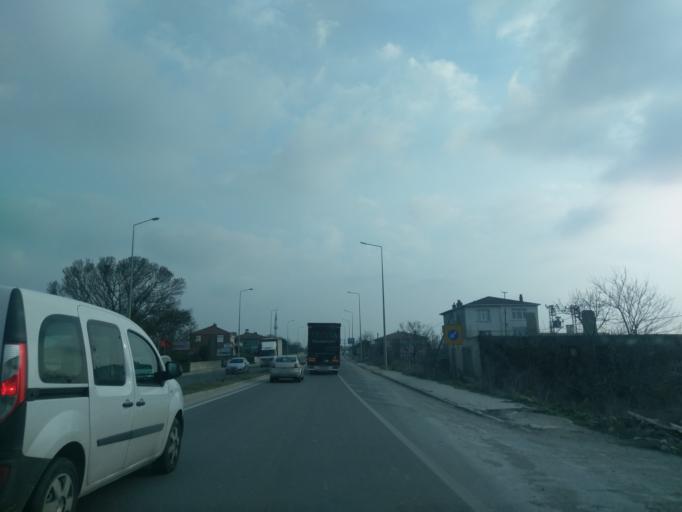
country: TR
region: Istanbul
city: Muratbey
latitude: 41.0913
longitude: 28.5136
